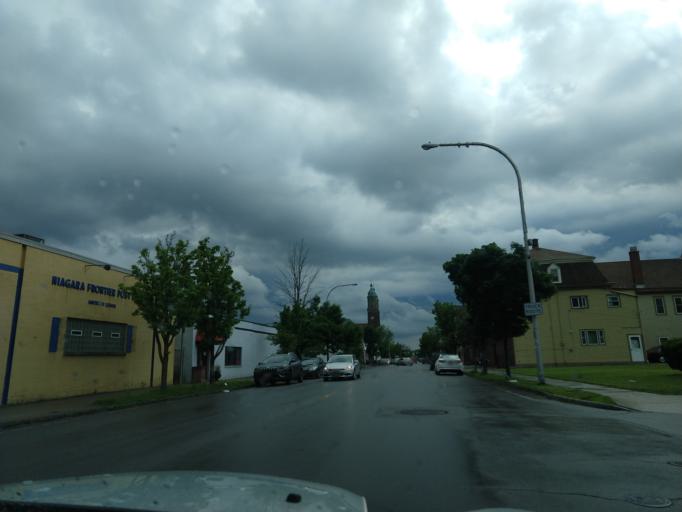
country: US
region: New York
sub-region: Erie County
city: Kenmore
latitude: 42.9402
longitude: -78.8846
